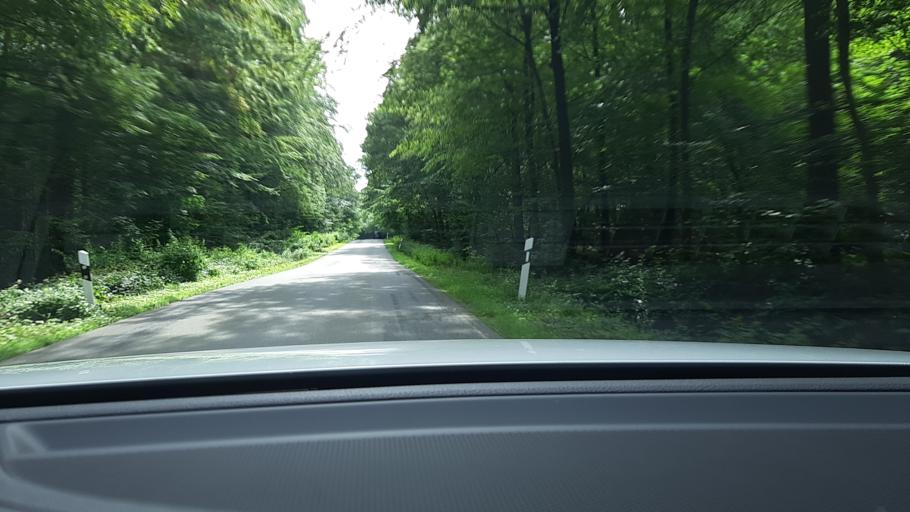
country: DE
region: Schleswig-Holstein
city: Reinfeld
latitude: 53.8507
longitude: 10.4730
